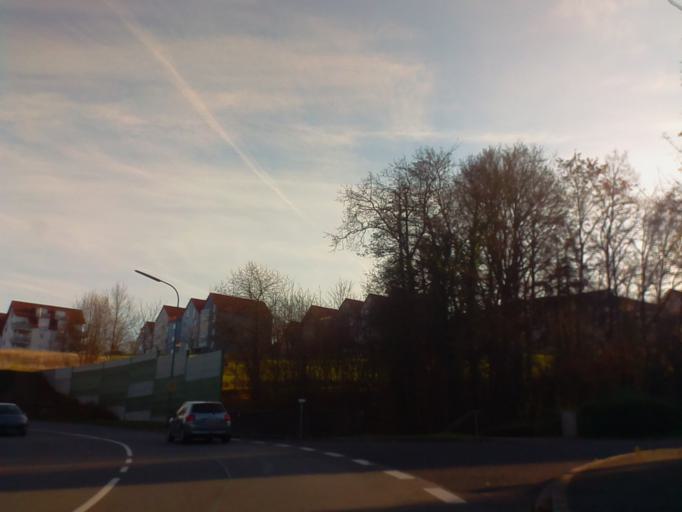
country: DE
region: Baden-Wuerttemberg
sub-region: Regierungsbezirk Stuttgart
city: Wertheim
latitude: 49.7536
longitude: 9.5083
